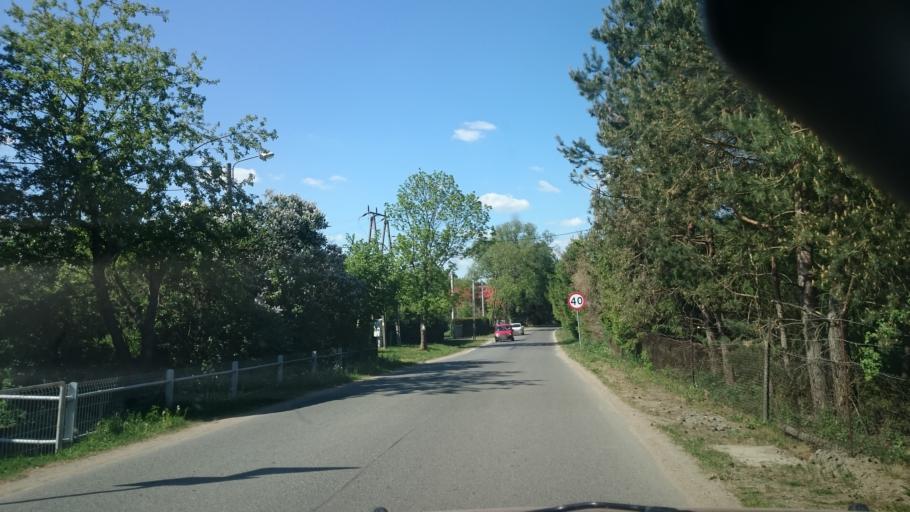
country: PL
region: Lower Silesian Voivodeship
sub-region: Powiat zabkowicki
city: Kamieniec Zabkowicki
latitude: 50.4981
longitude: 16.8319
